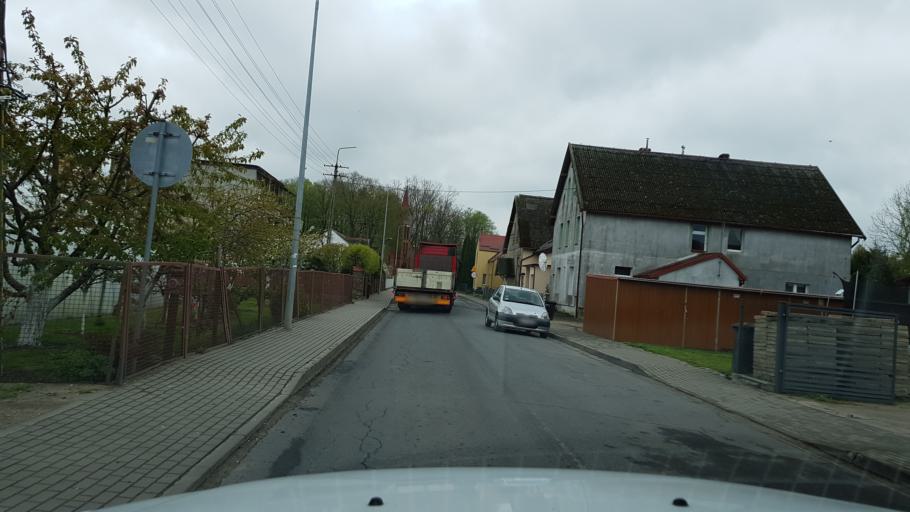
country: PL
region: West Pomeranian Voivodeship
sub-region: Powiat kolobrzeski
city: Ryman
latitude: 54.0287
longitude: 15.5303
